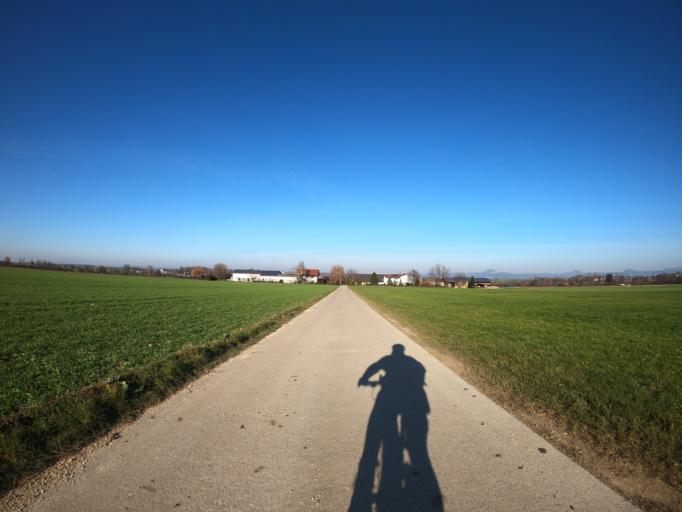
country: DE
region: Baden-Wuerttemberg
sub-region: Regierungsbezirk Stuttgart
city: Gammelshausen
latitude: 48.6468
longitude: 9.6524
